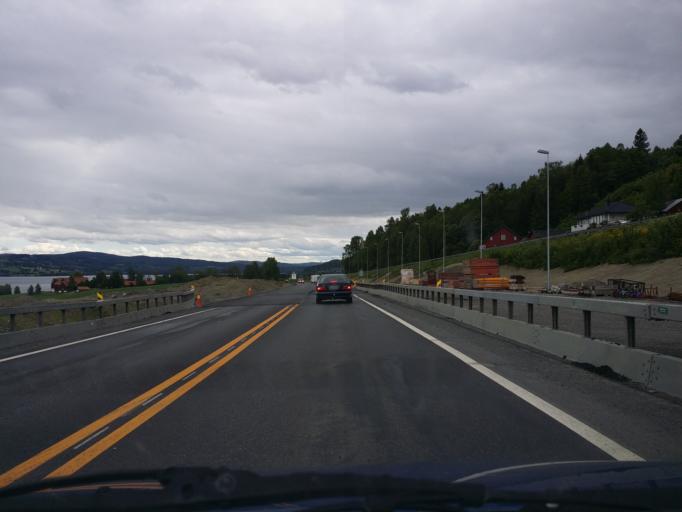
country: NO
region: Hedmark
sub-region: Ringsaker
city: Moelv
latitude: 60.9771
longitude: 10.5843
